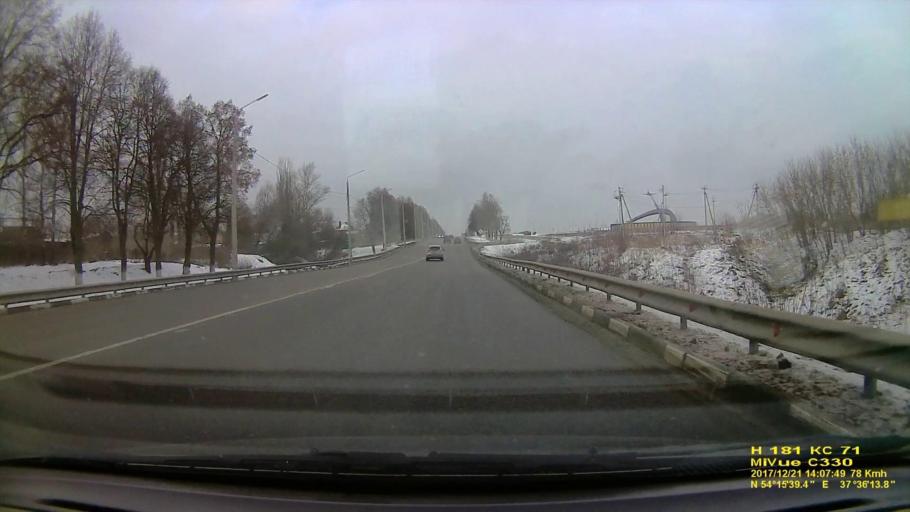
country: RU
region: Tula
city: Gorelki
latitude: 54.2611
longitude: 37.6037
